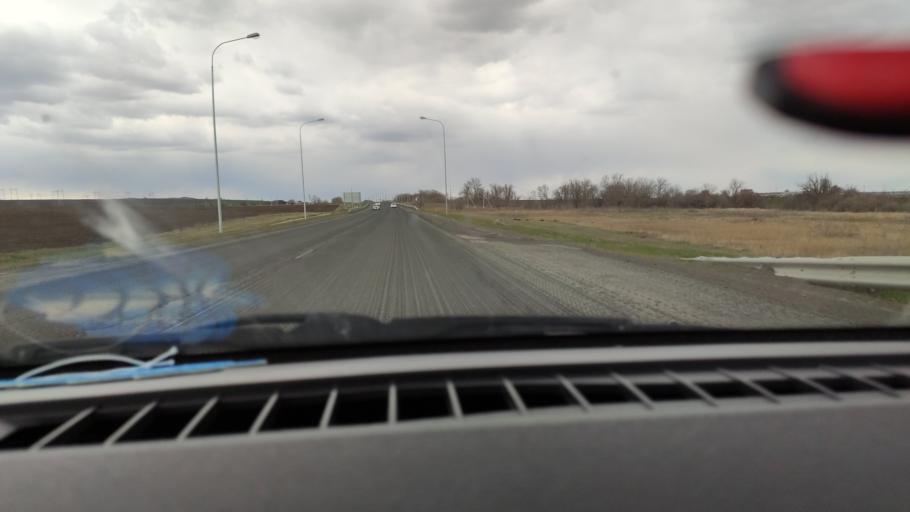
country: RU
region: Saratov
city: Yelshanka
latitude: 51.7925
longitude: 46.1589
